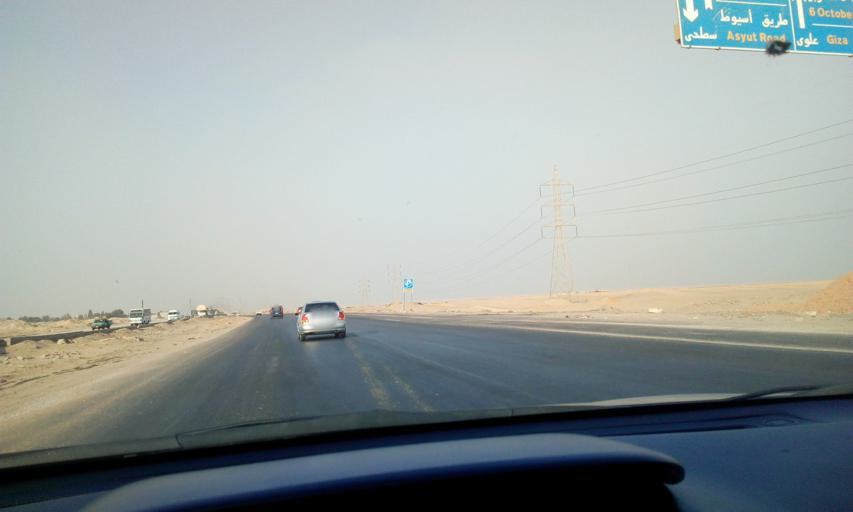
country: EG
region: Al Jizah
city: Madinat Sittah Uktubar
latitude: 29.8686
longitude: 31.0727
